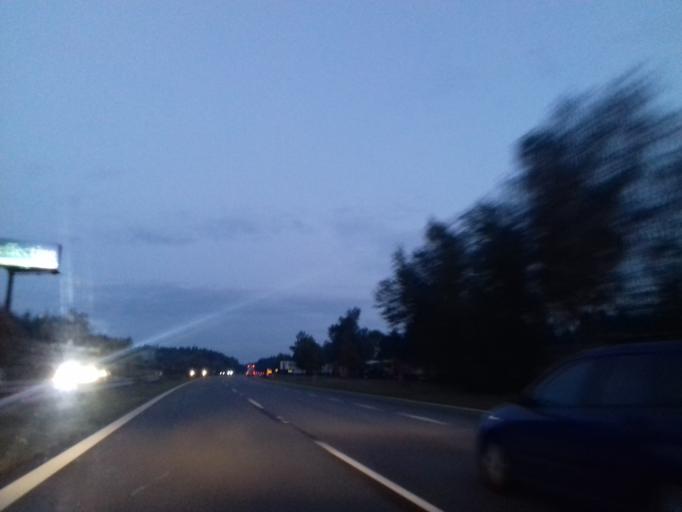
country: CZ
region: Vysocina
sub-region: Okres Pelhrimov
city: Zeliv
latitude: 49.5684
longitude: 15.2820
